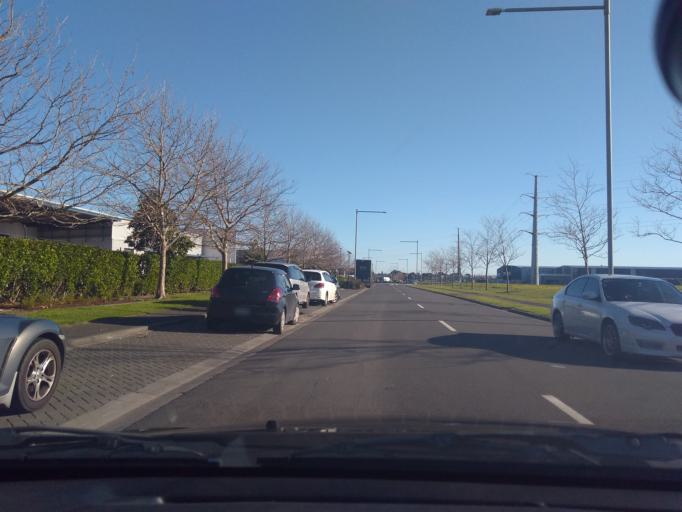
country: NZ
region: Auckland
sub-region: Auckland
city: Tamaki
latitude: -36.9290
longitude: 174.8758
